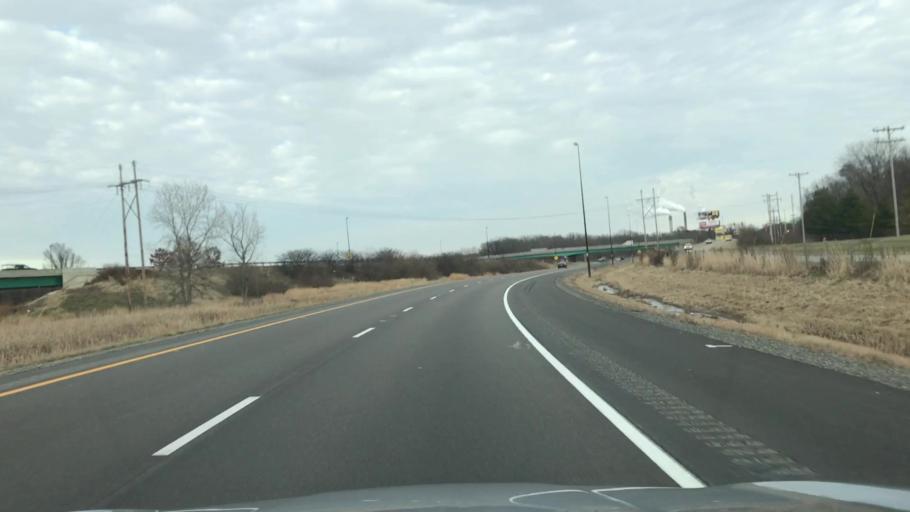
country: US
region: Illinois
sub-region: Sangamon County
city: Southern View
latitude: 39.7415
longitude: -89.6402
